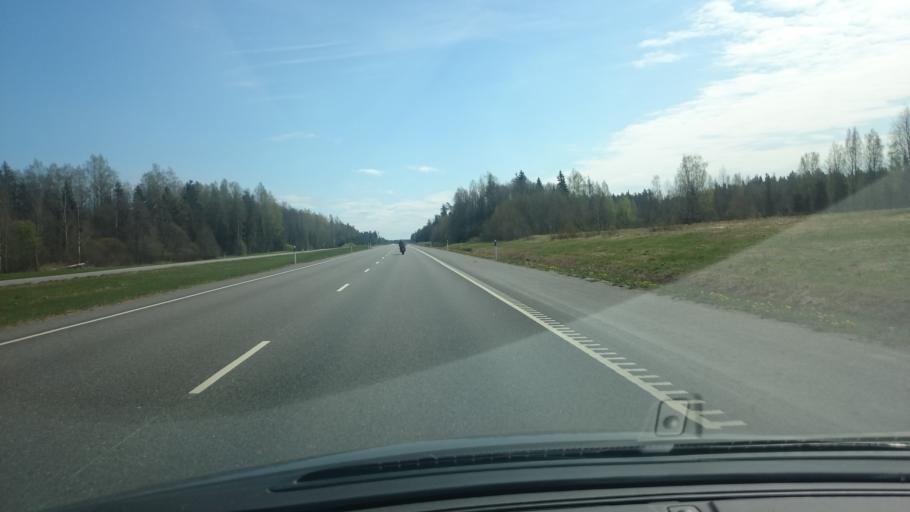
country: EE
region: Harju
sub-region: Loksa linn
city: Loksa
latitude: 59.4604
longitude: 25.7919
